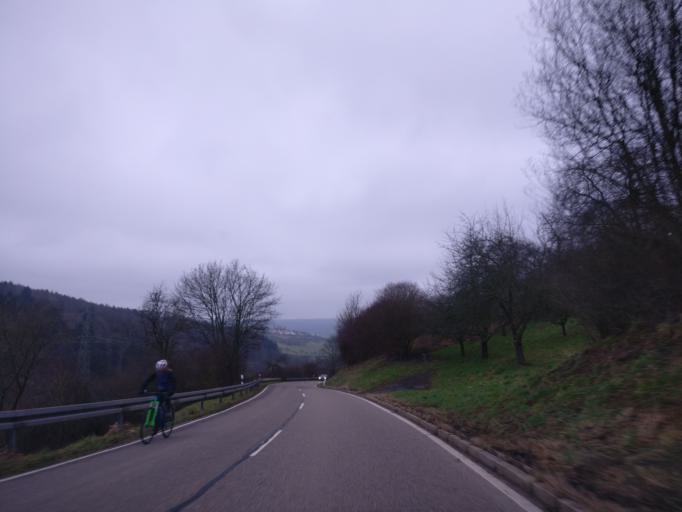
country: DE
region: Baden-Wuerttemberg
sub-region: Regierungsbezirk Stuttgart
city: Rudersberg
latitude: 48.8621
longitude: 9.4899
